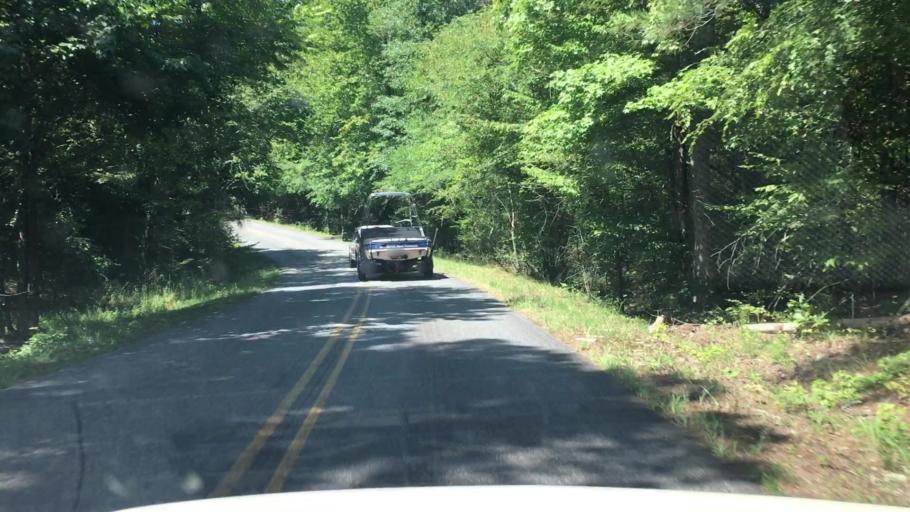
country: US
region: Arkansas
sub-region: Garland County
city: Piney
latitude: 34.5342
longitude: -93.3391
